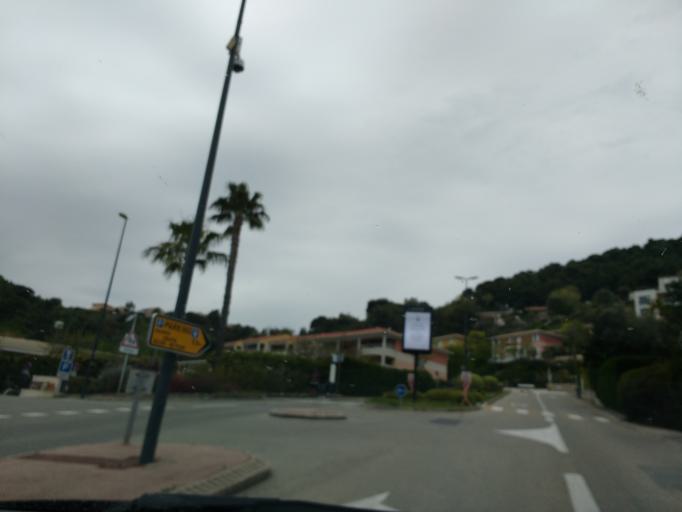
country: FR
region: Provence-Alpes-Cote d'Azur
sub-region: Departement des Alpes-Maritimes
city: Eze
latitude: 43.7339
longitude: 7.3525
